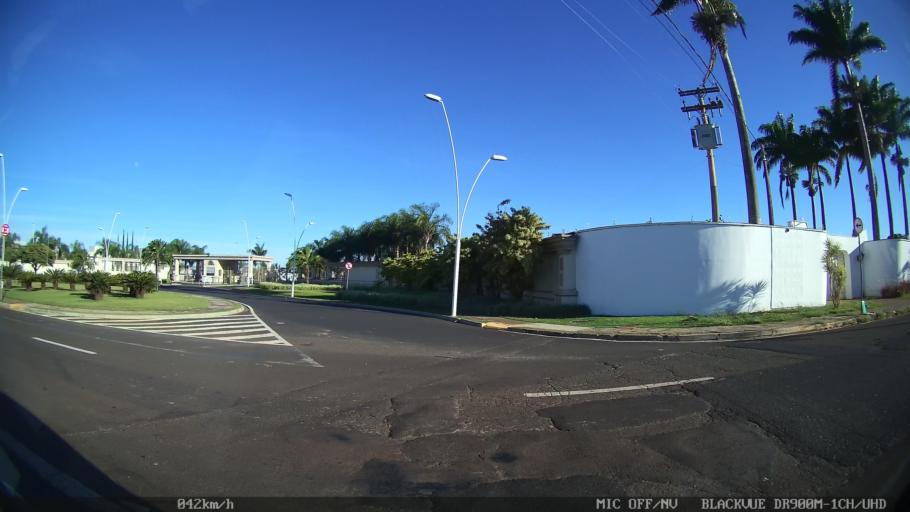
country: BR
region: Sao Paulo
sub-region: Franca
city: Franca
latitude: -20.5693
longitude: -47.4058
